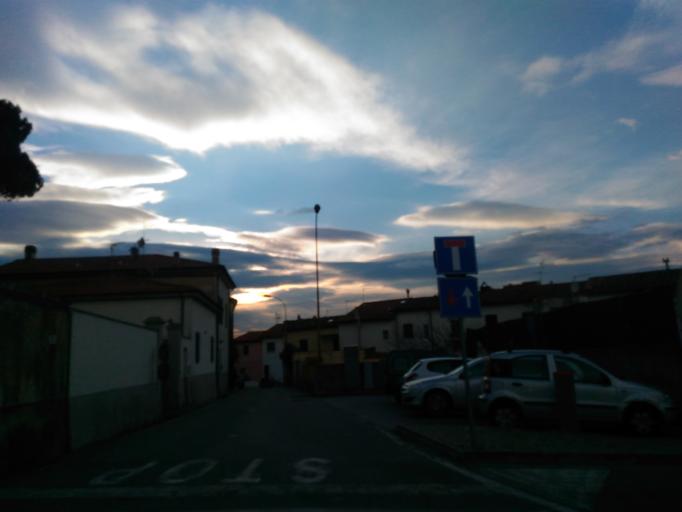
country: IT
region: Tuscany
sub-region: Provincia di Livorno
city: Collesalvetti
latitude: 43.5912
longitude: 10.4759
